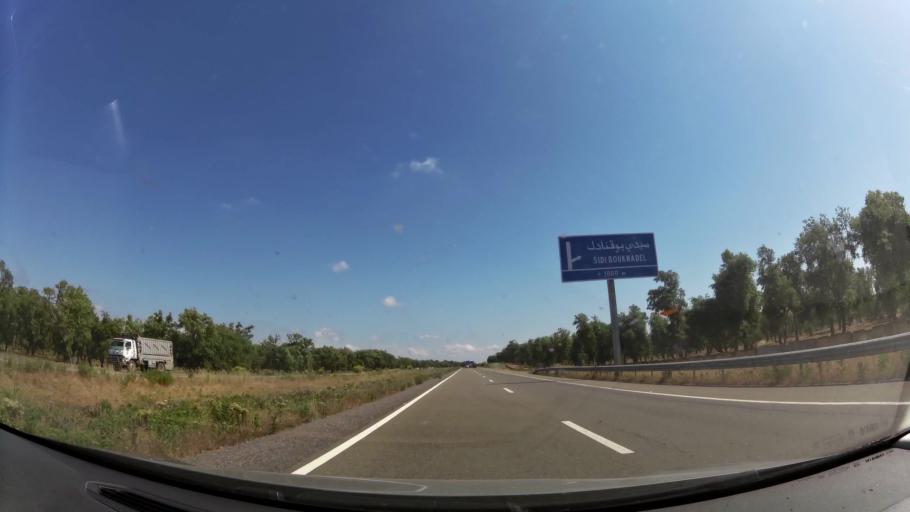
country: MA
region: Rabat-Sale-Zemmour-Zaer
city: Sale
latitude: 34.1093
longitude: -6.6864
